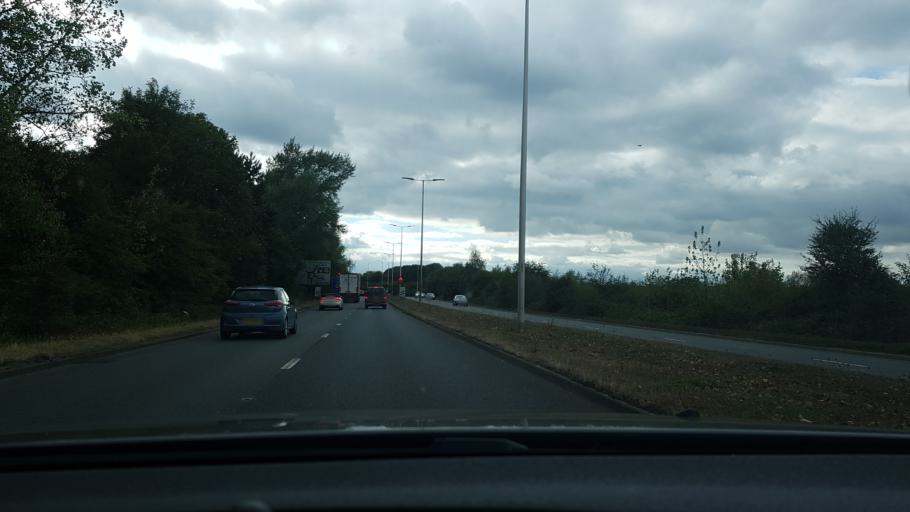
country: GB
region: England
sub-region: West Berkshire
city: Theale
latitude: 51.4316
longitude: -1.0863
